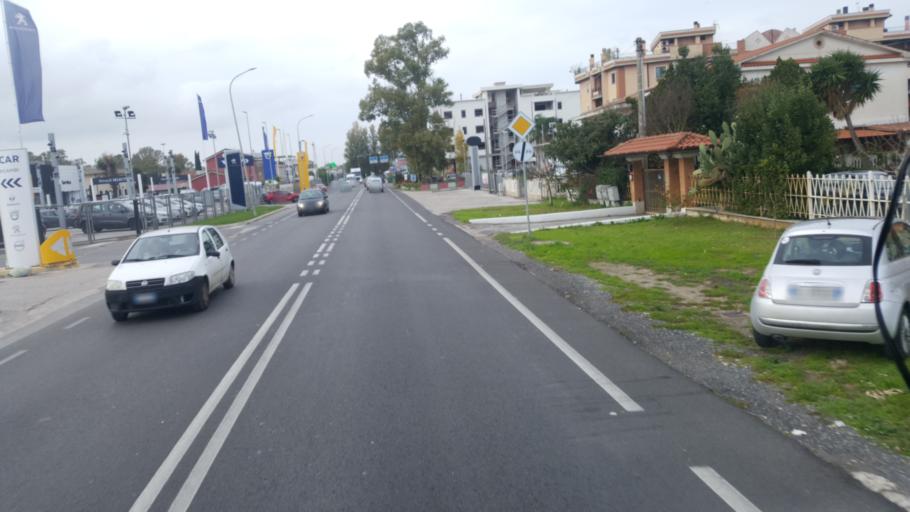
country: IT
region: Latium
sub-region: Provincia di Latina
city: Borgo Podgora
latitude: 41.4806
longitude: 12.8674
